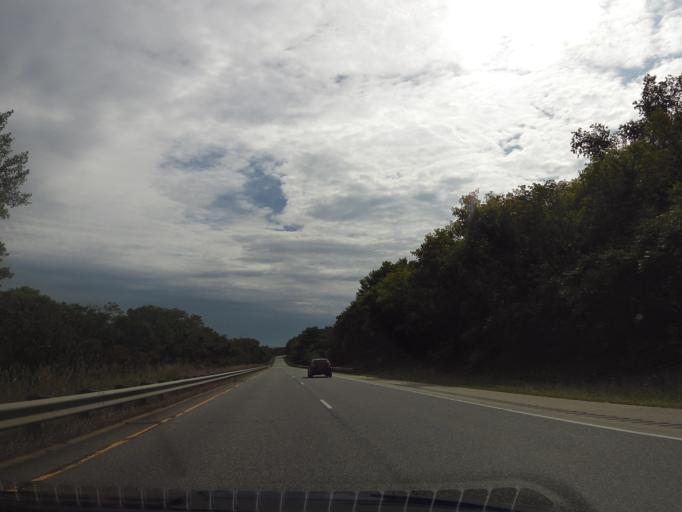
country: US
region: Wisconsin
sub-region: La Crosse County
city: Brice Prairie
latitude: 43.9211
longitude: -91.3939
